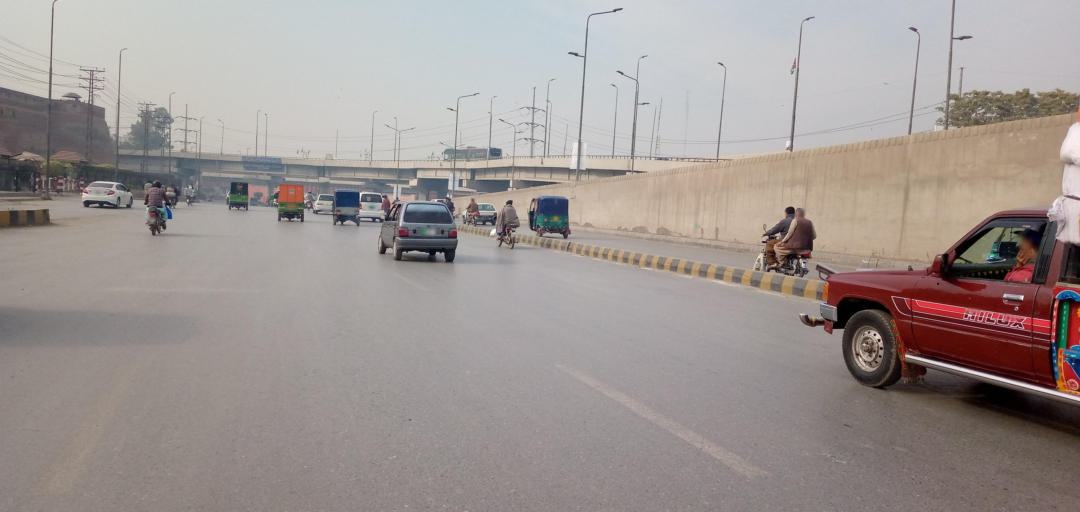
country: PK
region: Khyber Pakhtunkhwa
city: Peshawar
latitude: 34.0144
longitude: 71.5709
